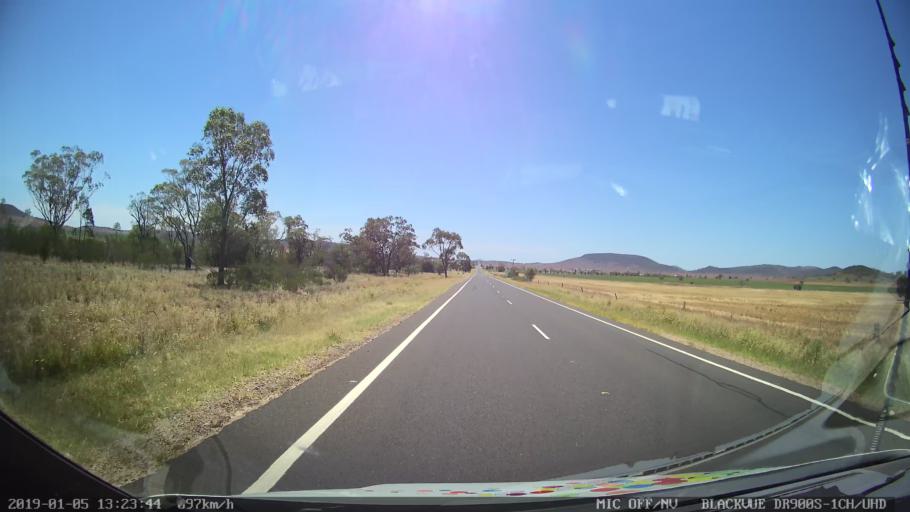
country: AU
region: New South Wales
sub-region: Gunnedah
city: Gunnedah
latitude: -31.0755
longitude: 149.9792
